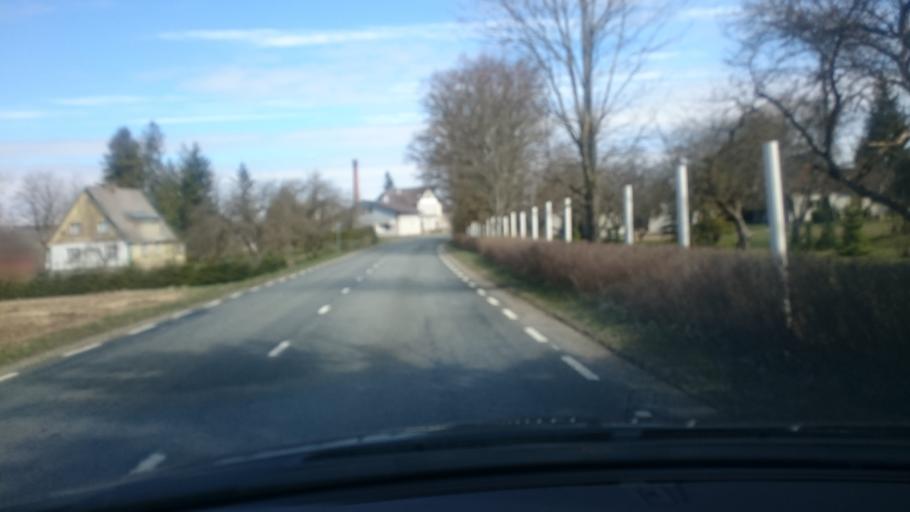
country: EE
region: Harju
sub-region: Raasiku vald
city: Raasiku
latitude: 59.1166
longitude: 25.1692
